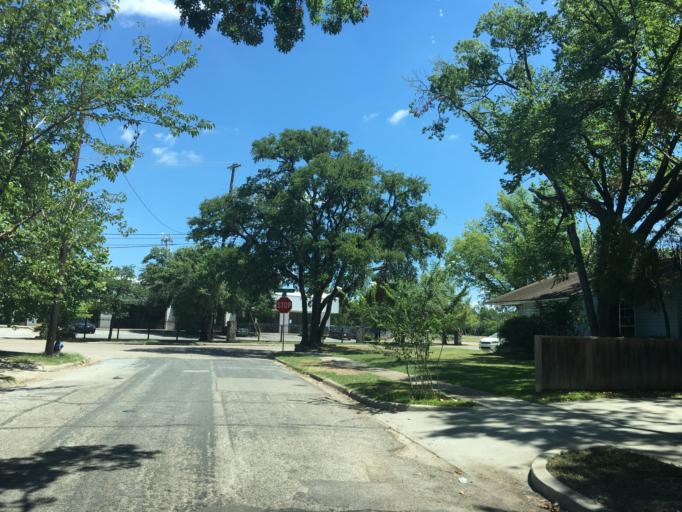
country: US
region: Texas
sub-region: Dallas County
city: Garland
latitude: 32.8422
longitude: -96.6866
